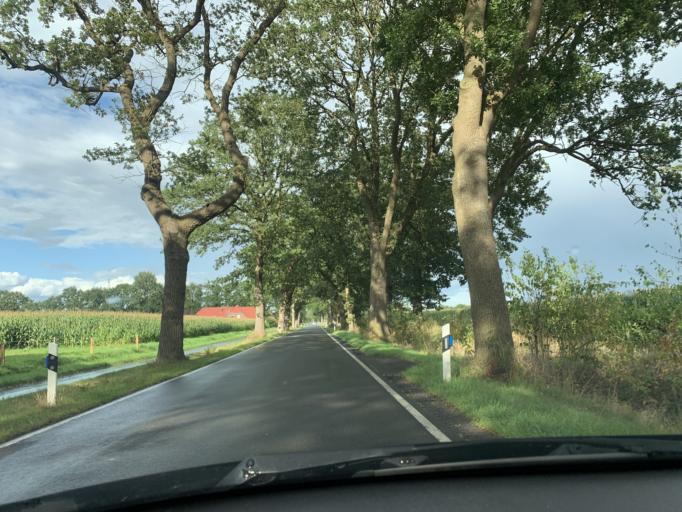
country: DE
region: Lower Saxony
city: Bockhorn
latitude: 53.3103
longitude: 8.0061
